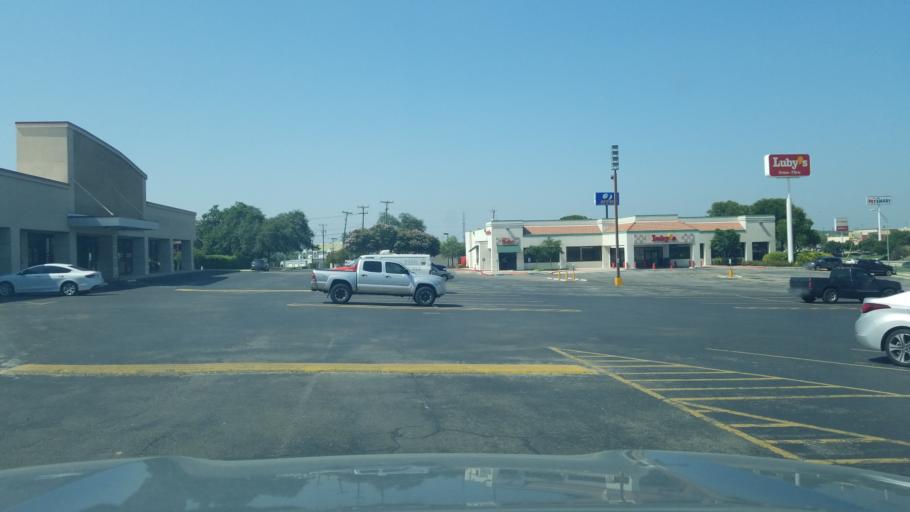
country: US
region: Texas
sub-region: Bexar County
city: Hollywood Park
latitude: 29.5619
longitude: -98.4819
